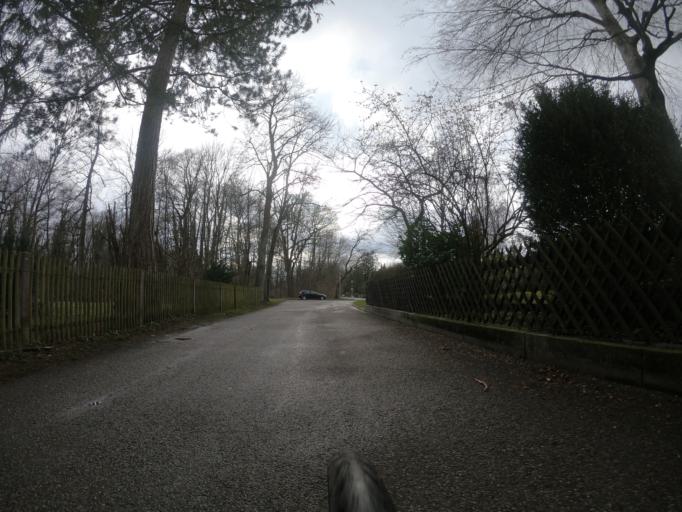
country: DE
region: Bavaria
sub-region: Upper Bavaria
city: Fuerstenfeldbruck
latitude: 48.1797
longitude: 11.2670
